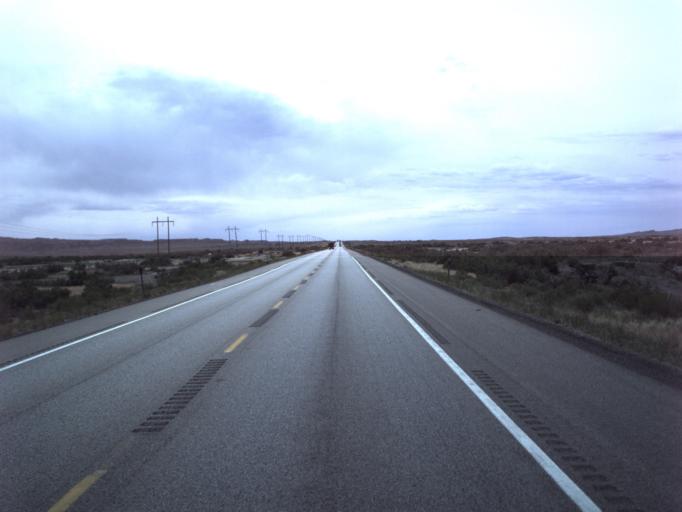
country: US
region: Utah
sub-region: Carbon County
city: East Carbon City
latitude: 39.2406
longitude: -110.3389
